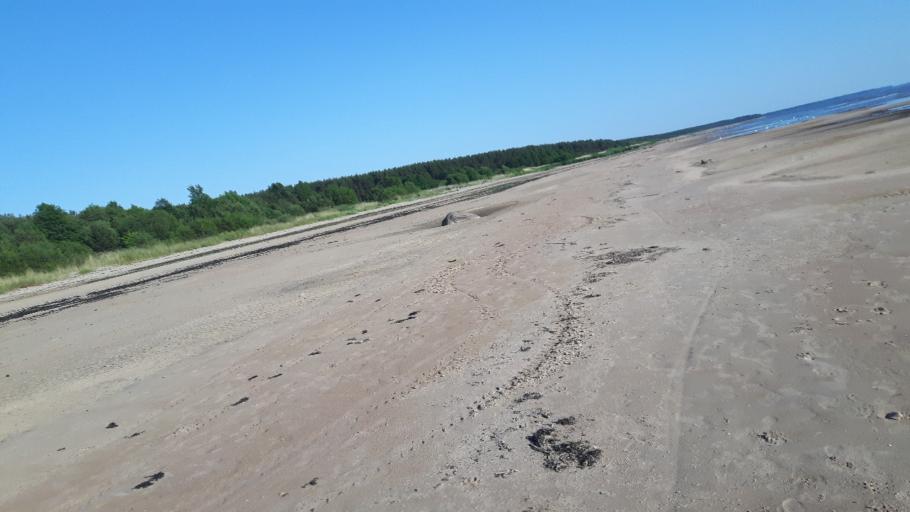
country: LV
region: Salacgrivas
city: Salacgriva
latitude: 57.6883
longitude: 24.3557
